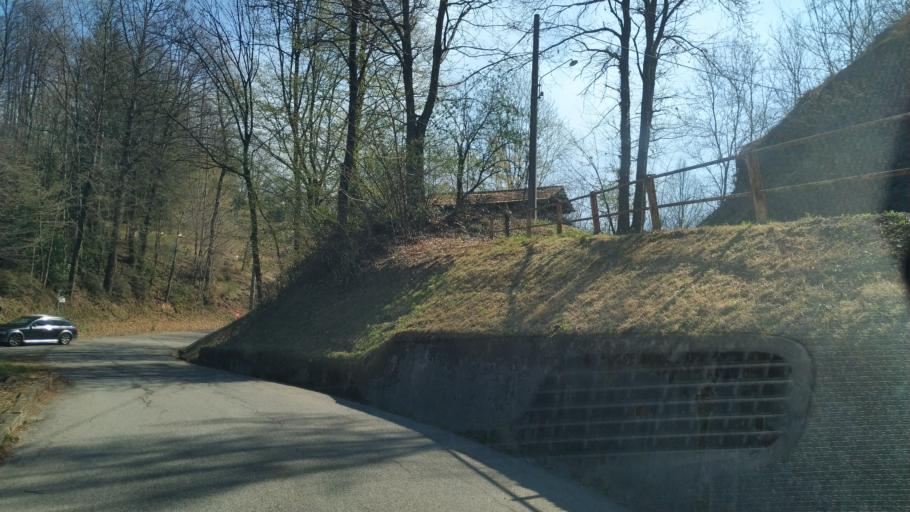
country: IT
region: Piedmont
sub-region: Provincia di Biella
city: Pray
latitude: 45.6803
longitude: 8.2056
